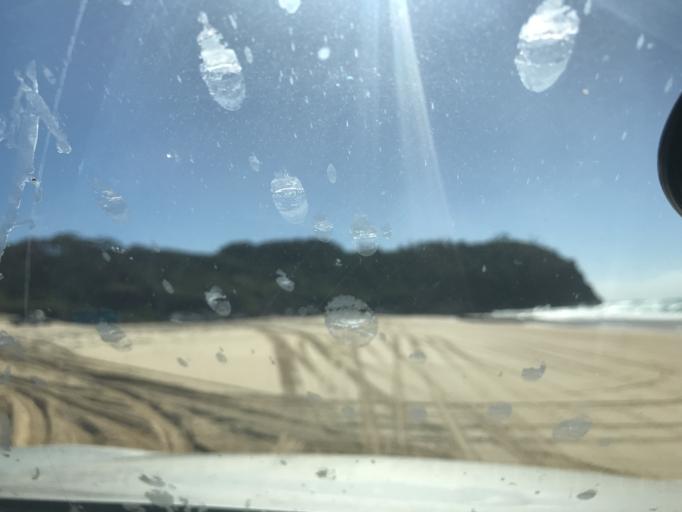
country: AU
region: Queensland
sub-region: Fraser Coast
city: Urangan
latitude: -25.0142
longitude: 153.3573
